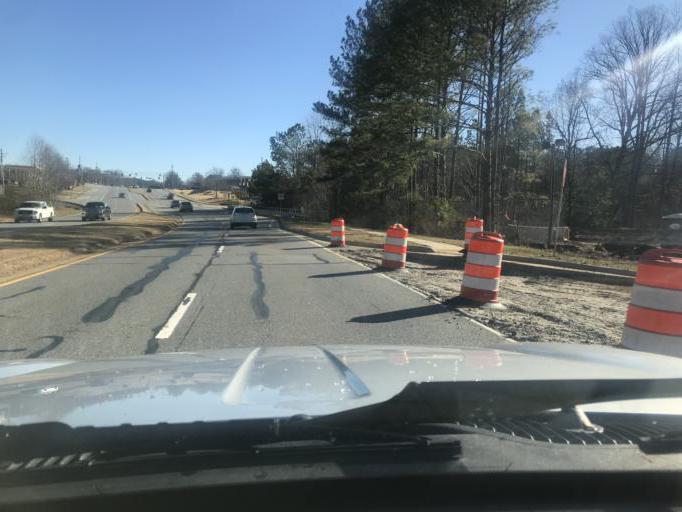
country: US
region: Georgia
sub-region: Gwinnett County
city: Lawrenceville
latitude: 33.9676
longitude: -84.0391
